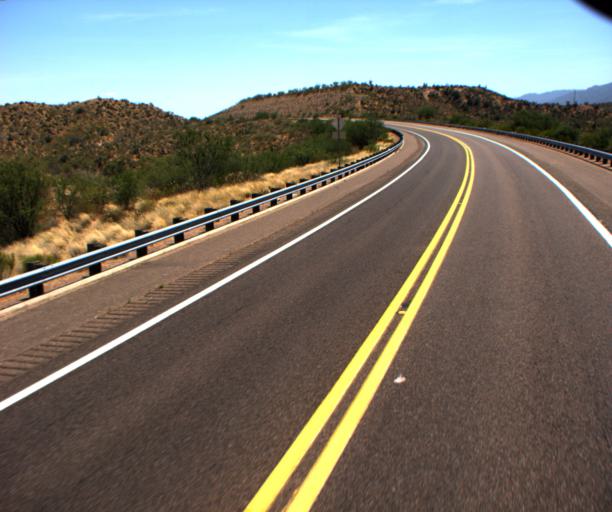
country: US
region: Arizona
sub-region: Gila County
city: Tonto Basin
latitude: 33.9227
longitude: -111.3181
